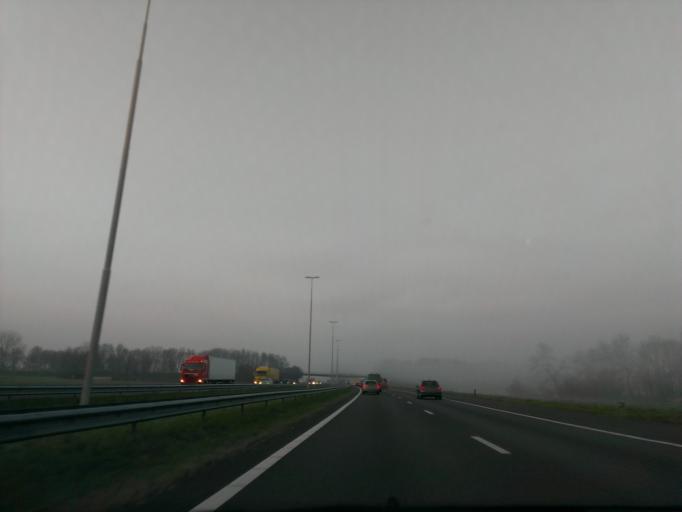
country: NL
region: Gelderland
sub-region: Gemeente Epe
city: Vaassen
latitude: 52.2700
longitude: 6.0028
